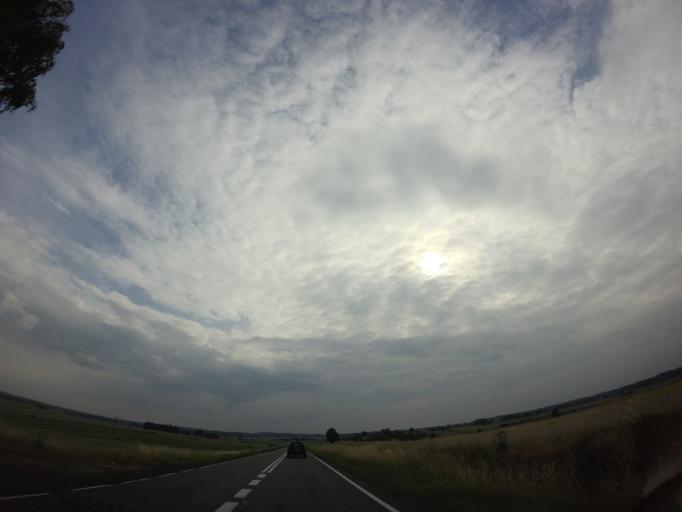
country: PL
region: West Pomeranian Voivodeship
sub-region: Powiat szczecinecki
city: Szczecinek
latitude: 53.6534
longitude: 16.6512
